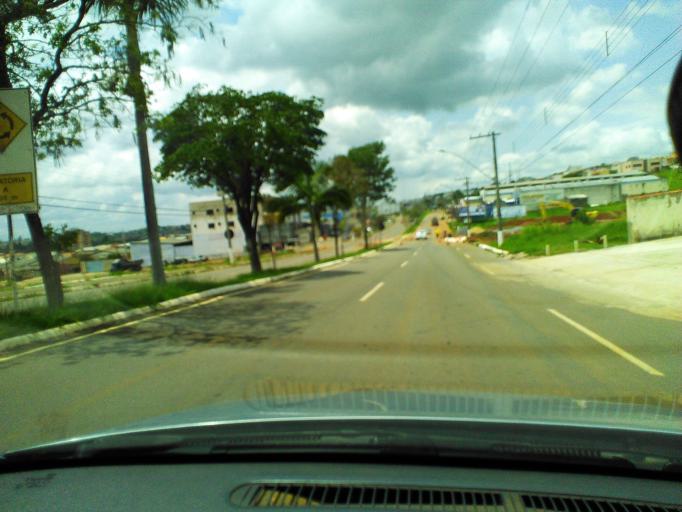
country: BR
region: Minas Gerais
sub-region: Tres Coracoes
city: Tres Coracoes
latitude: -21.6748
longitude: -45.2704
